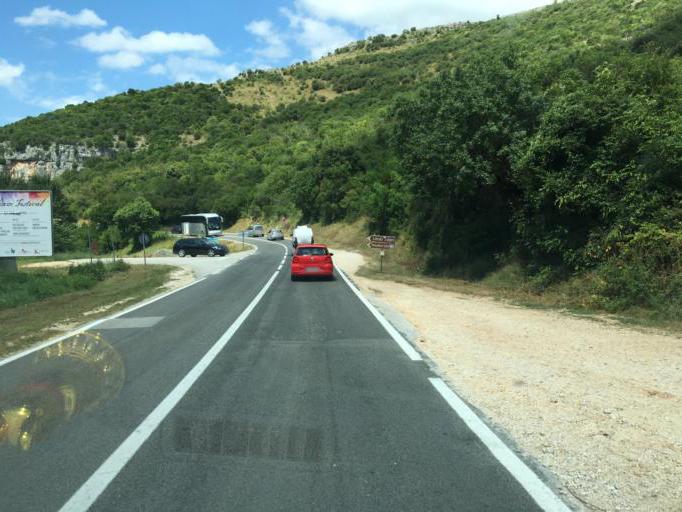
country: HR
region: Istarska
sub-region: Grad Rovinj
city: Rovinj
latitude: 45.1283
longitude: 13.7441
